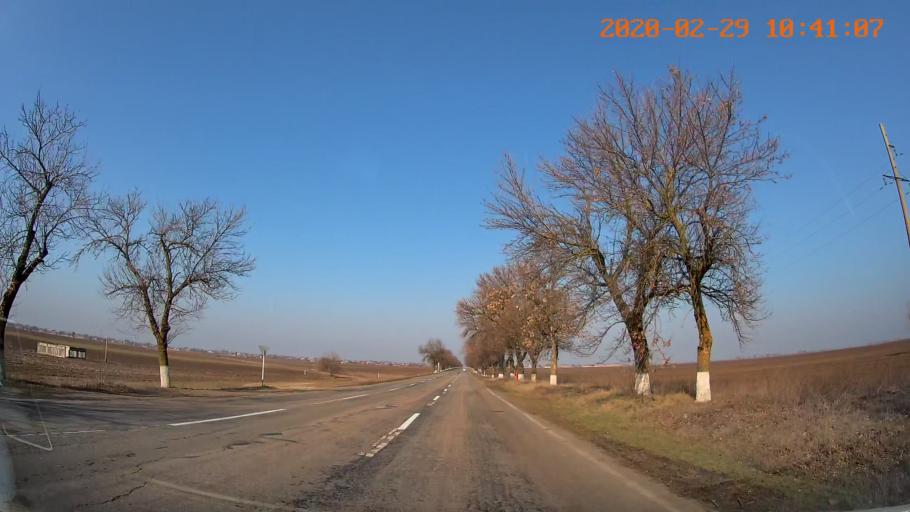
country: MD
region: Telenesti
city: Grigoriopol
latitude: 47.0394
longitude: 29.4298
